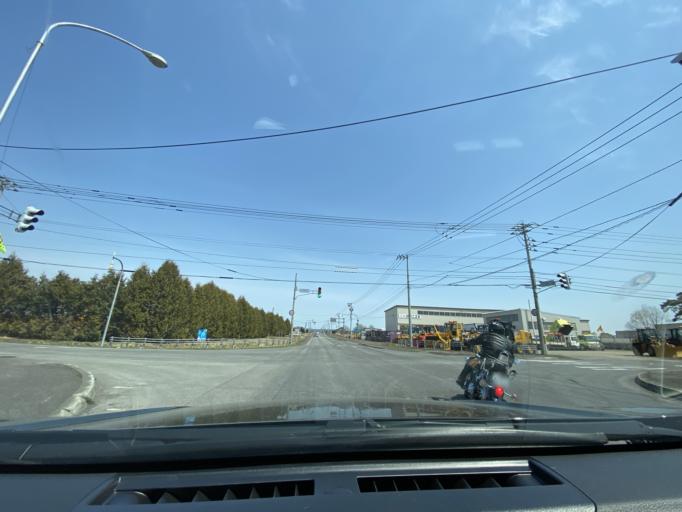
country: JP
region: Hokkaido
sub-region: Asahikawa-shi
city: Asahikawa
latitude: 43.8688
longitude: 142.4859
